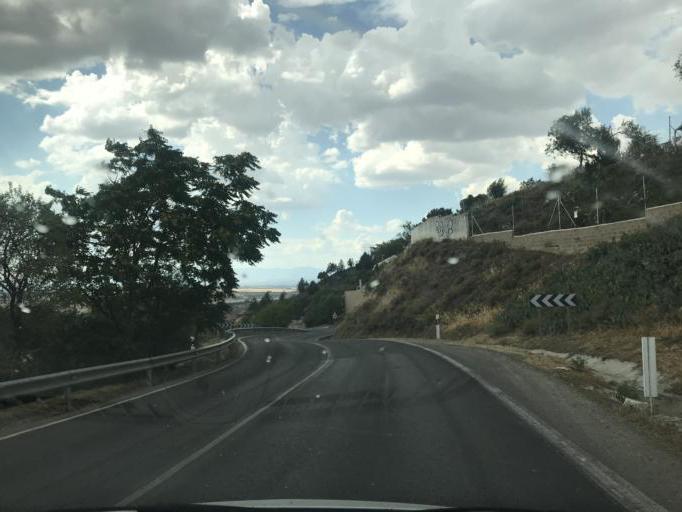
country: ES
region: Madrid
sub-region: Provincia de Madrid
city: Paracuellos de Jarama
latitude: 40.5039
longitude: -3.5329
